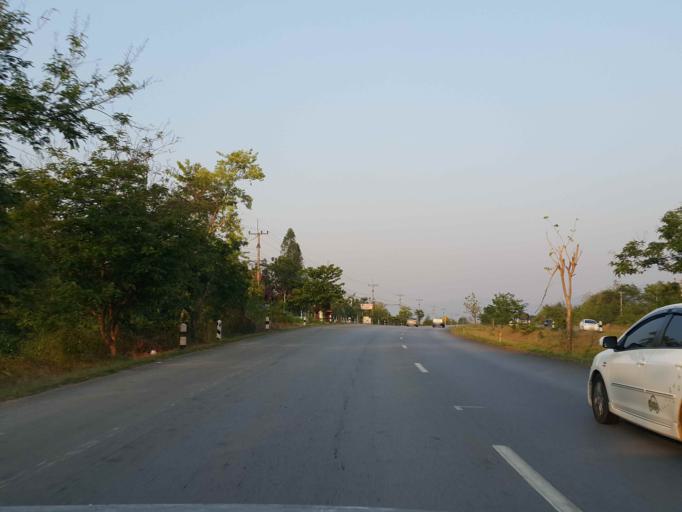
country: TH
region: Lampang
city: Sop Prap
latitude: 17.8615
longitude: 99.3146
